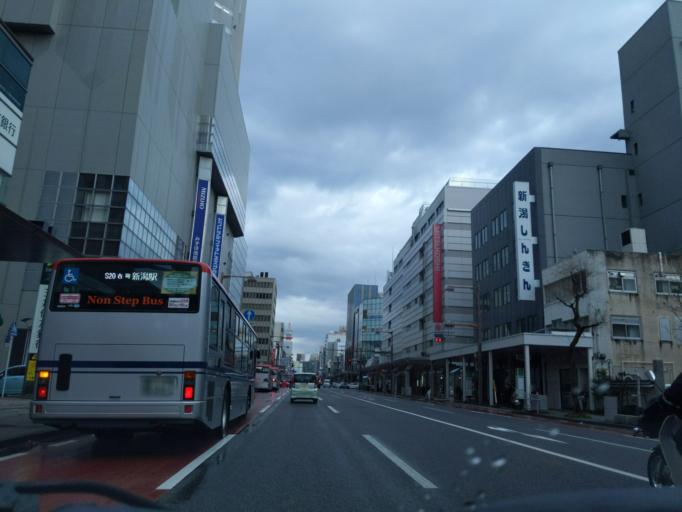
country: JP
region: Niigata
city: Niigata-shi
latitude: 37.9224
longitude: 139.0422
